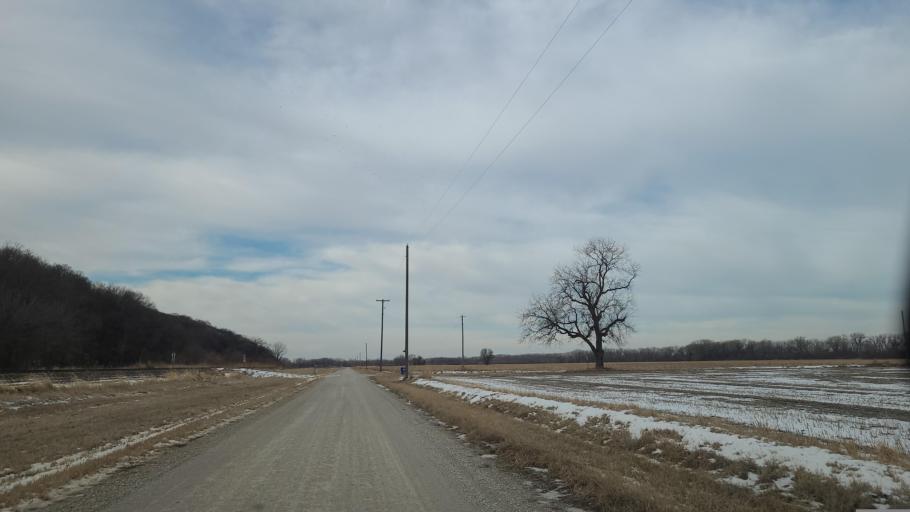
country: US
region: Kansas
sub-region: Jefferson County
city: Oskaloosa
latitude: 39.0608
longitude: -95.4456
